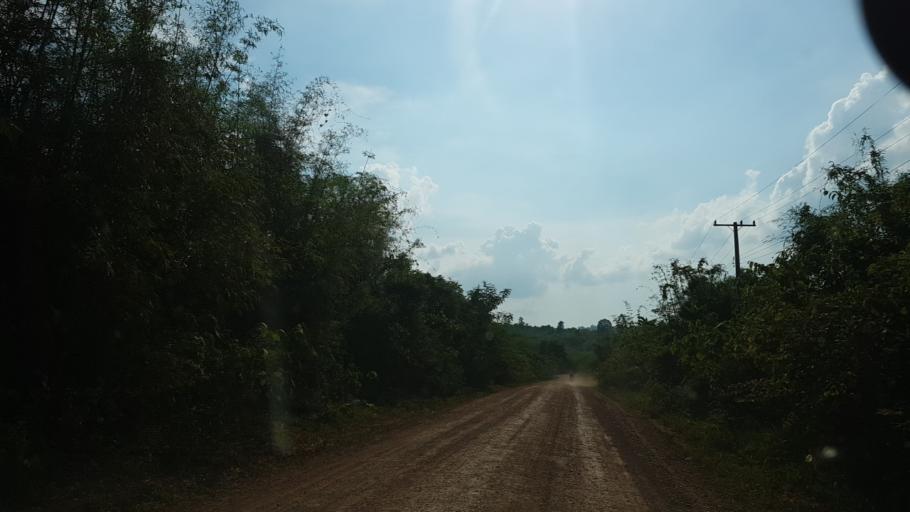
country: LA
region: Vientiane
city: Muang Phon-Hong
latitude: 18.3472
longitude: 102.2864
